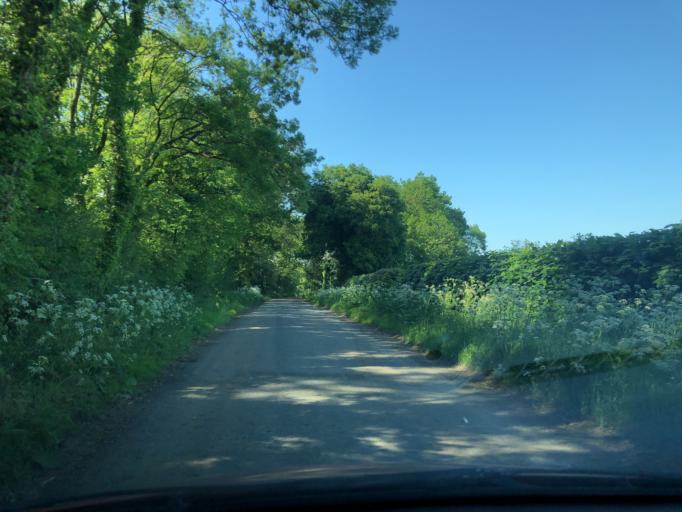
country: GB
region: England
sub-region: North Yorkshire
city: Northallerton
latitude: 54.3117
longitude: -1.3824
